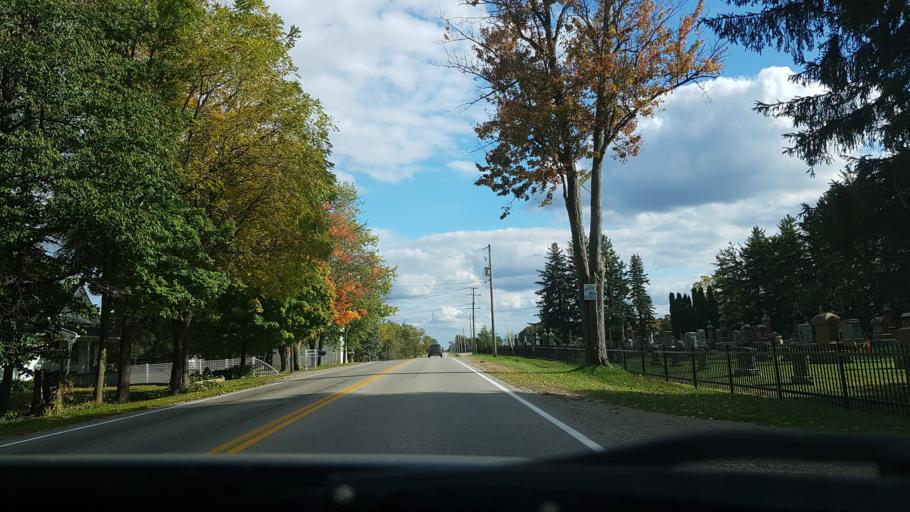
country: CA
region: Ontario
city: Delaware
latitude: 43.0295
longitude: -81.4615
